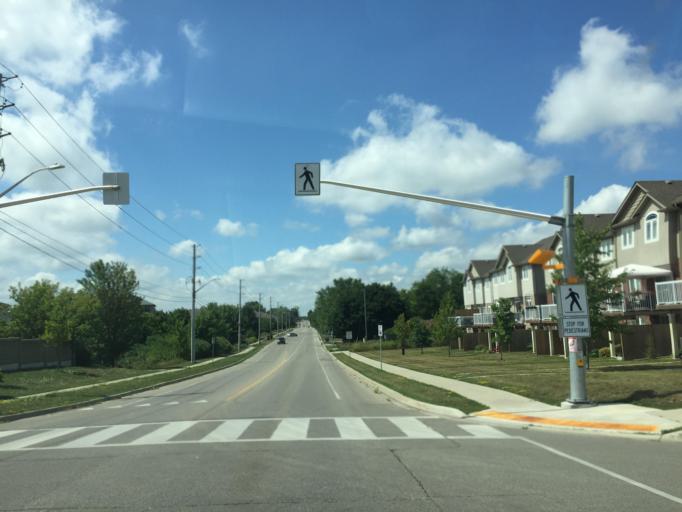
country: CA
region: Ontario
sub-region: Wellington County
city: Guelph
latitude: 43.5203
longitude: -80.1908
